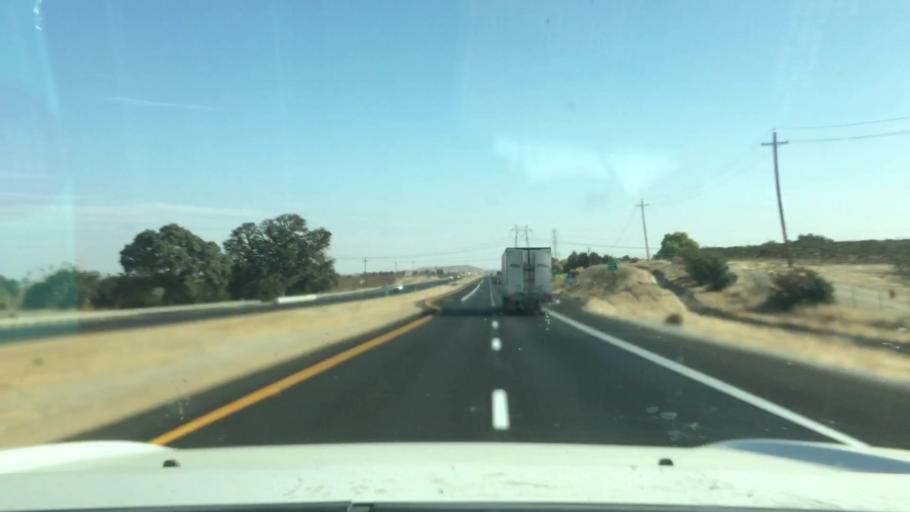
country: US
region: California
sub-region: San Luis Obispo County
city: Paso Robles
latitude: 35.6593
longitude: -120.5825
